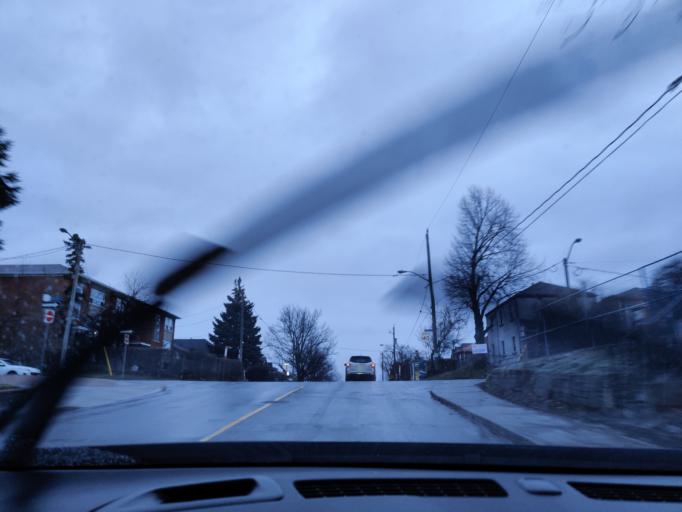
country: CA
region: Ontario
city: Toronto
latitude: 43.6870
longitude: -79.4597
